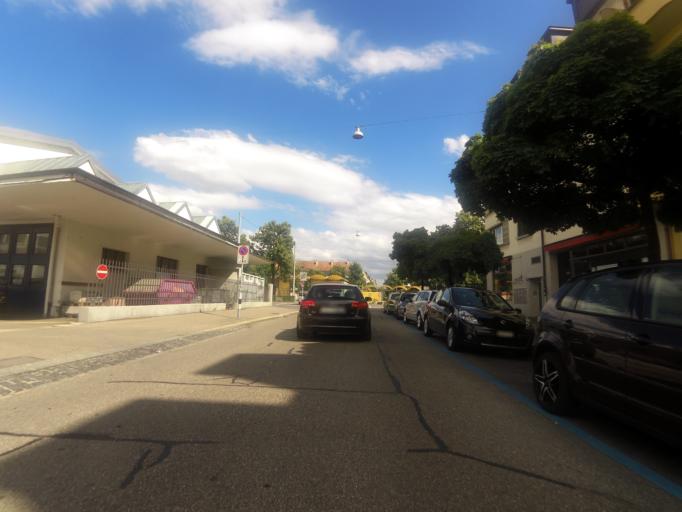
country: CH
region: Zurich
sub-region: Bezirk Zuerich
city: Zuerich (Kreis 3) / Sihlfeld
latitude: 47.3767
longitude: 8.5112
